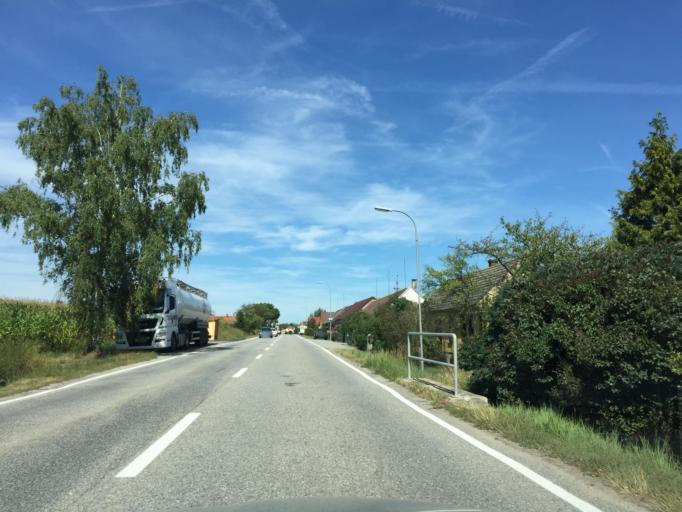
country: CZ
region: Jihocesky
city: Sevetin
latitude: 49.0852
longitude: 14.5419
